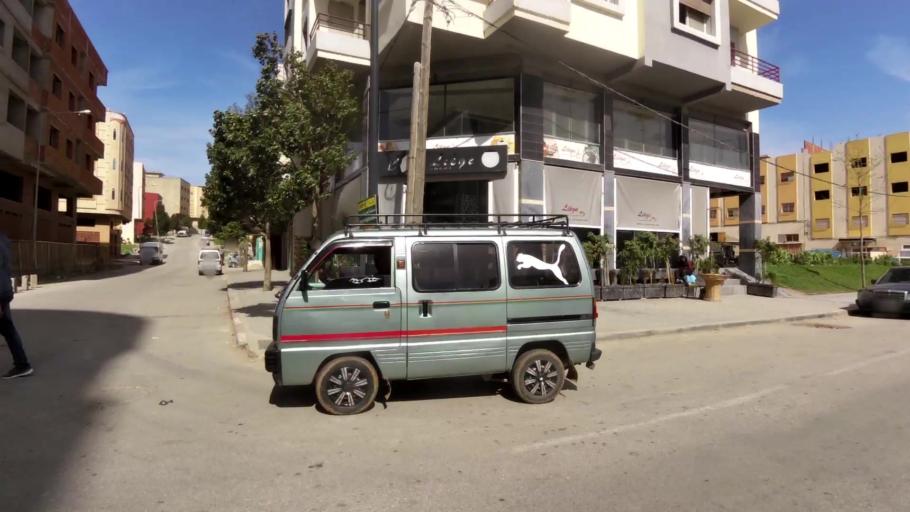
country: MA
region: Tanger-Tetouan
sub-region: Tanger-Assilah
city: Tangier
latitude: 35.7261
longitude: -5.8041
